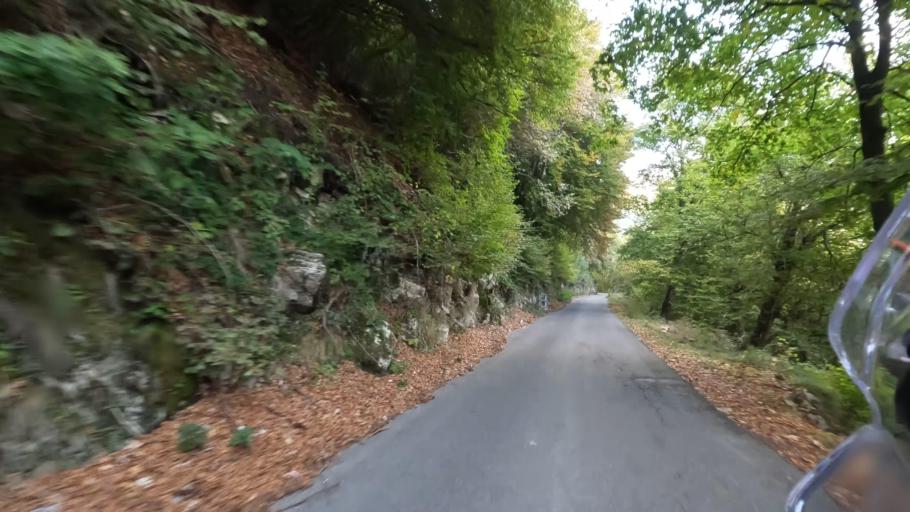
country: IT
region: Lombardy
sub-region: Provincia di Como
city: Pigra
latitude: 45.9730
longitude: 9.1241
